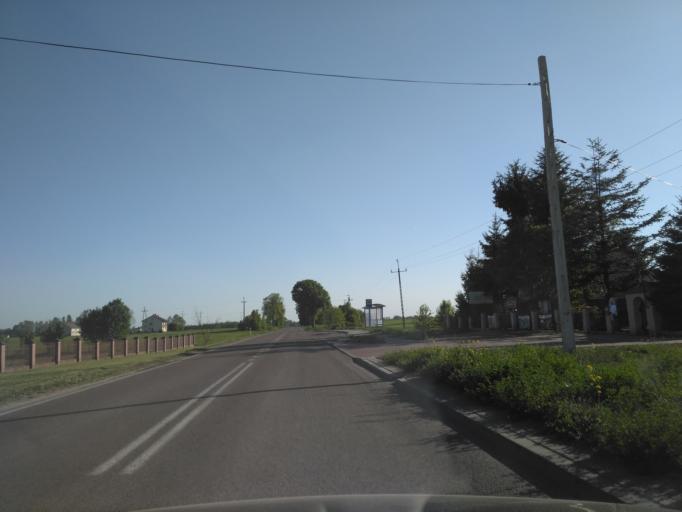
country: PL
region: Lublin Voivodeship
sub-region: Powiat swidnicki
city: Trawniki
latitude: 51.2067
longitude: 23.0687
